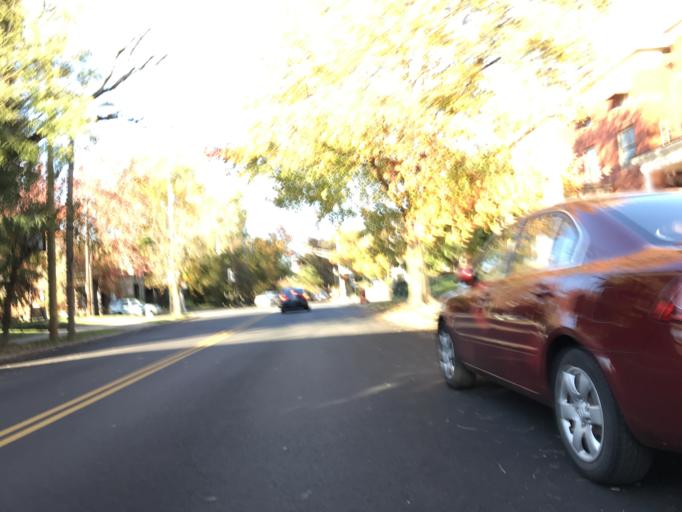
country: US
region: Kentucky
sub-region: Jefferson County
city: Louisville
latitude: 38.2228
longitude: -85.7624
